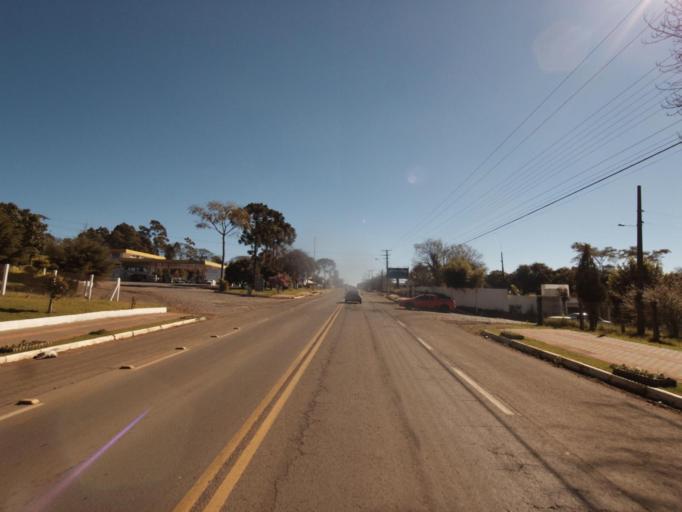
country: AR
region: Misiones
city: Bernardo de Irigoyen
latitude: -26.7515
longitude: -53.5131
